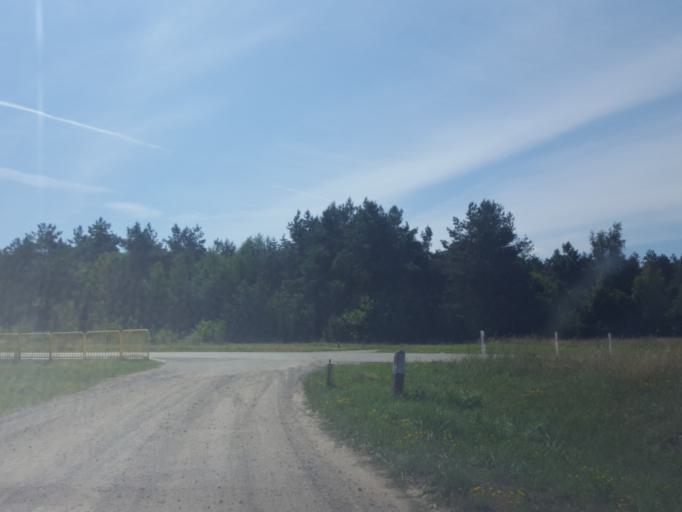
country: PL
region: Podlasie
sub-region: Powiat kolnenski
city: Stawiski
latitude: 53.3640
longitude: 22.1544
